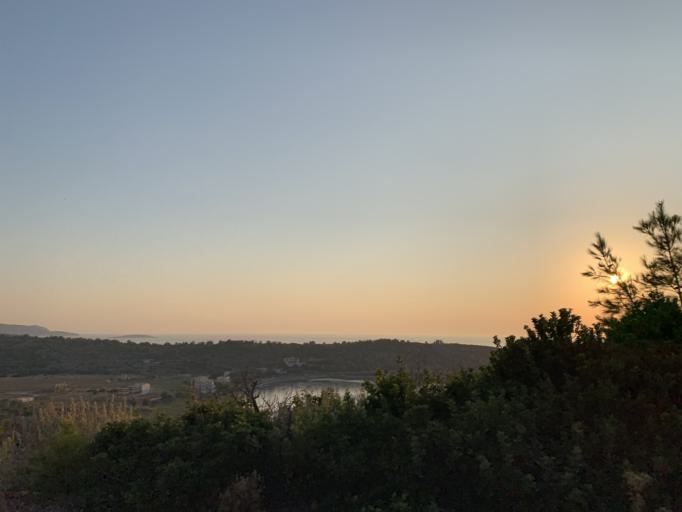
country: GR
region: North Aegean
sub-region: Chios
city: Thymiana
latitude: 38.3423
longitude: 25.9989
